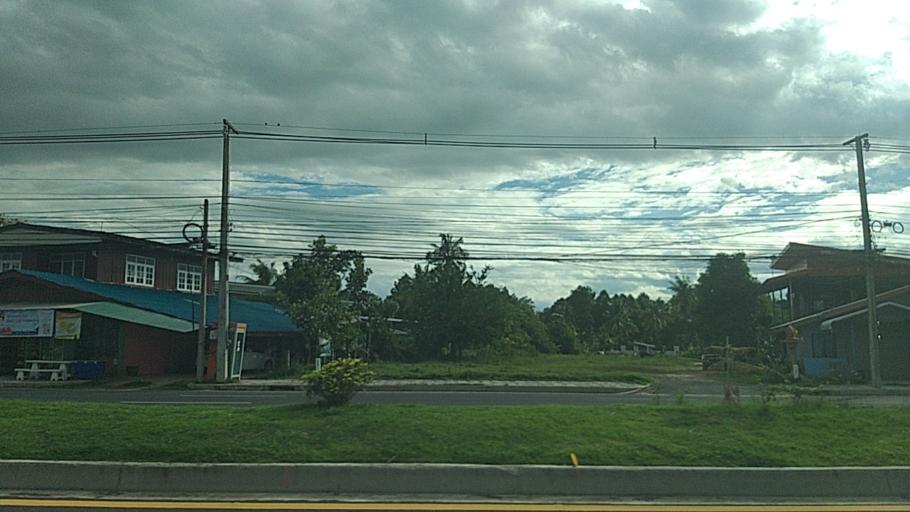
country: TH
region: Surin
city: Prasat
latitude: 14.6177
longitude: 103.4149
